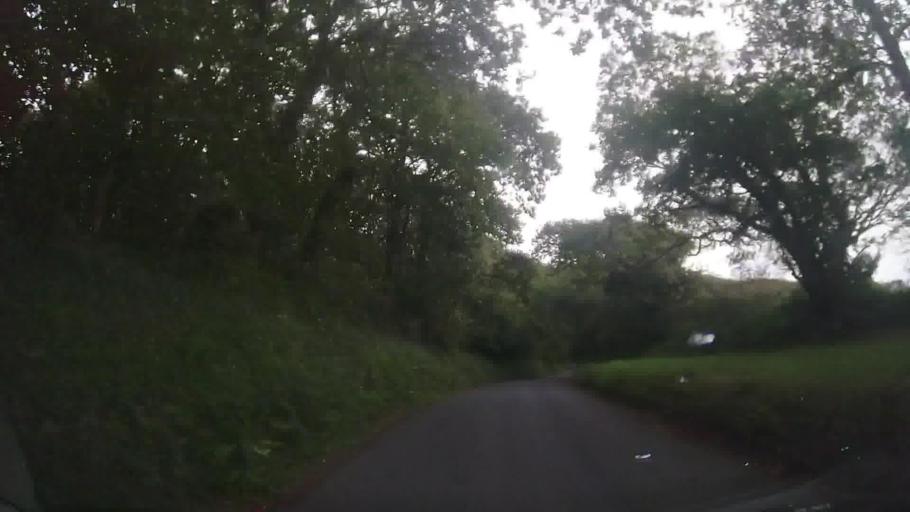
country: GB
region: Wales
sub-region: Pembrokeshire
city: Saundersfoot
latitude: 51.7400
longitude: -4.6313
